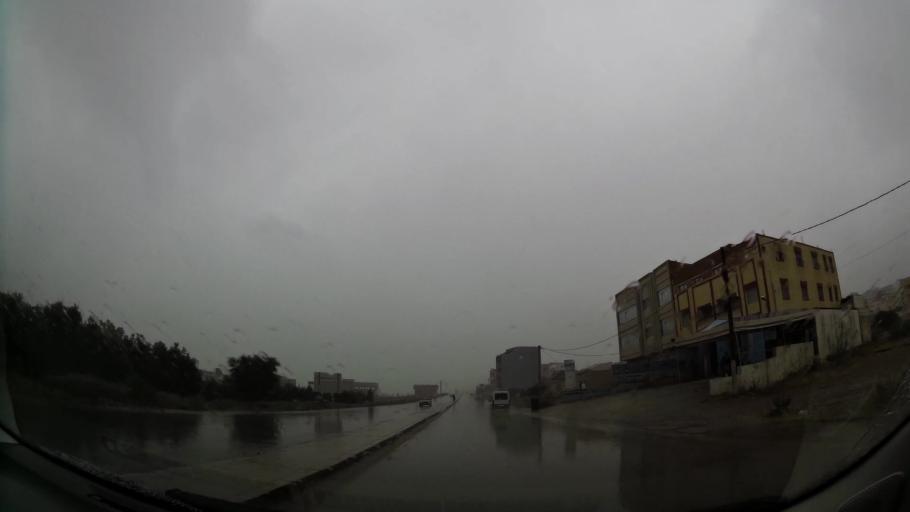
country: MA
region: Taza-Al Hoceima-Taounate
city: Imzourene
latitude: 35.1353
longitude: -3.8469
